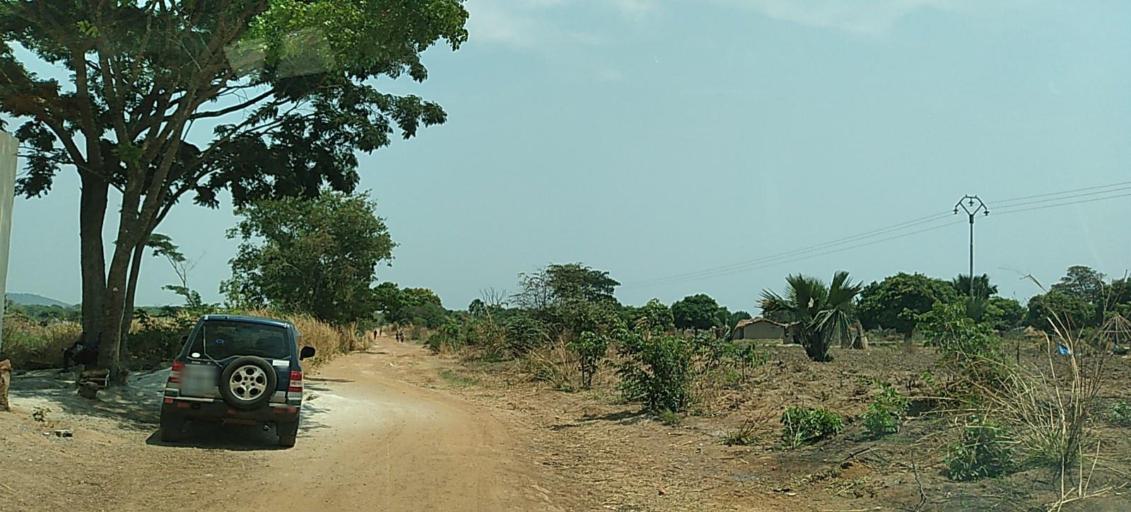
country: ZM
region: Copperbelt
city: Ndola
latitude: -13.0646
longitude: 28.7404
